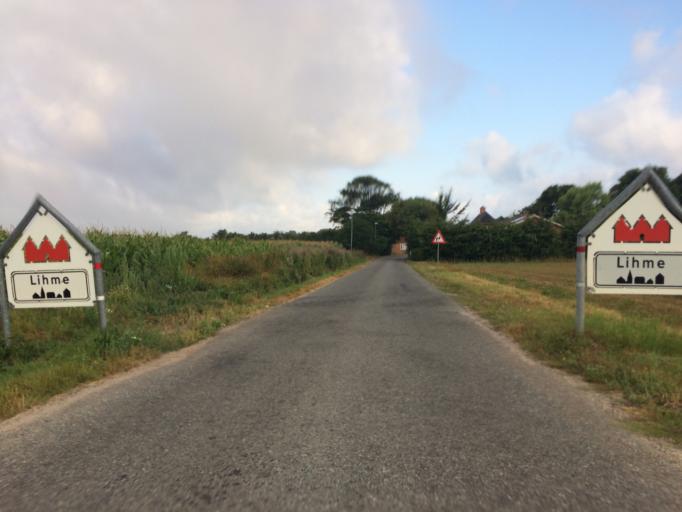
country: DK
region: Central Jutland
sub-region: Holstebro Kommune
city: Vinderup
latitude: 56.5957
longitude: 8.7332
